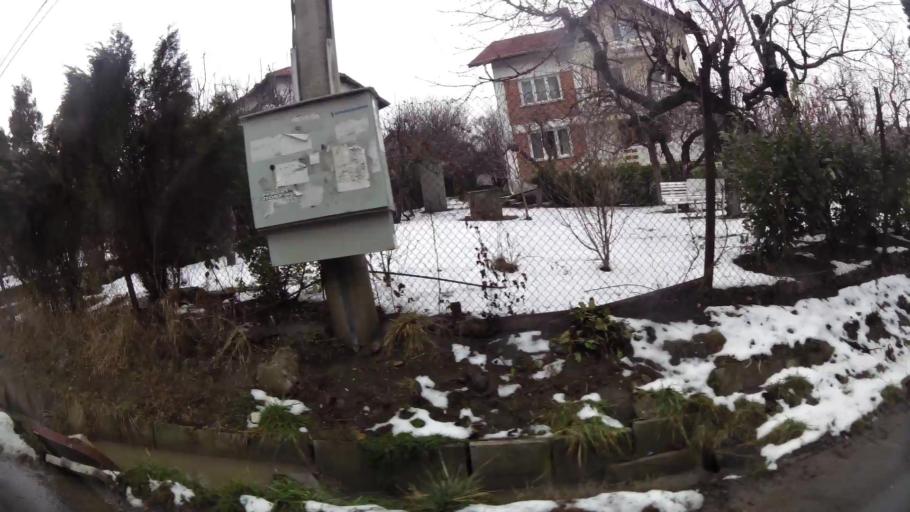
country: BG
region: Sofiya
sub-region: Obshtina Bozhurishte
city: Bozhurishte
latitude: 42.6731
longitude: 23.2335
